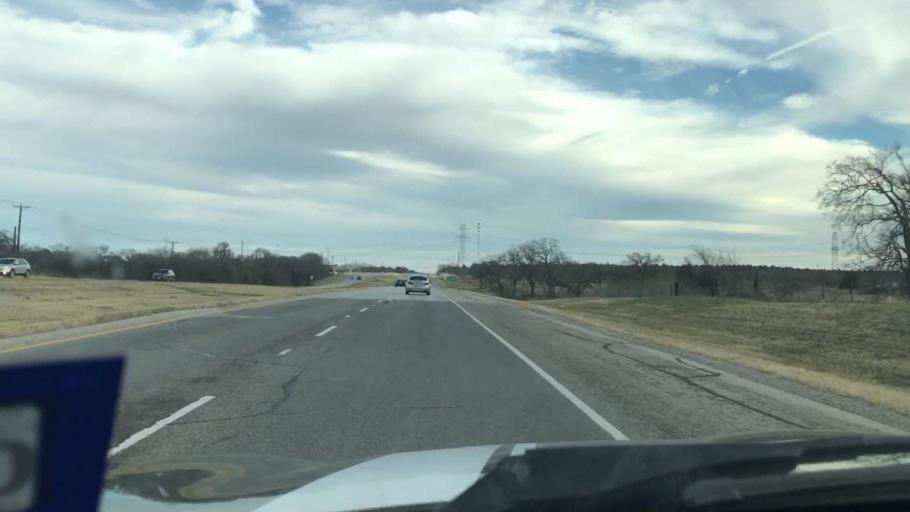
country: US
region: Texas
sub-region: Bastrop County
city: Elgin
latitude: 30.3325
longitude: -97.3535
